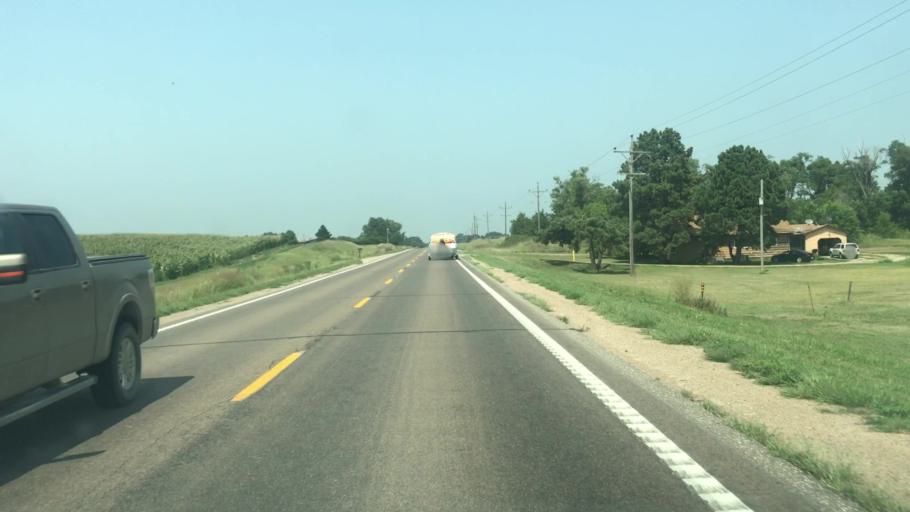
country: US
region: Nebraska
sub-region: Hall County
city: Wood River
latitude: 41.0217
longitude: -98.6074
